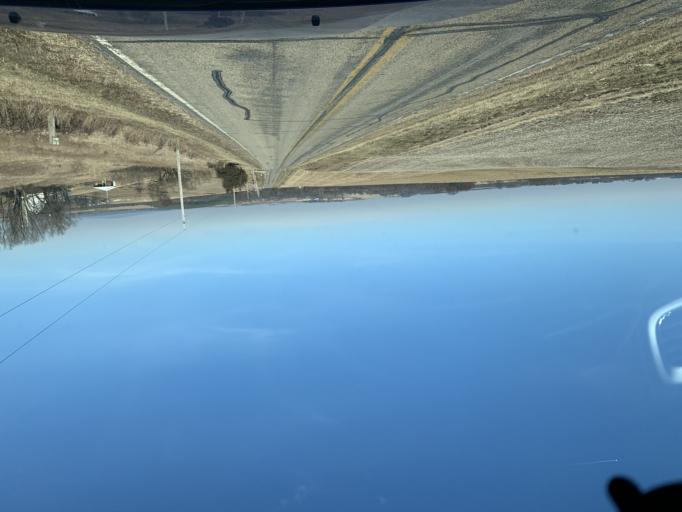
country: US
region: Wisconsin
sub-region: Iowa County
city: Barneveld
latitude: 42.8297
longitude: -89.9314
